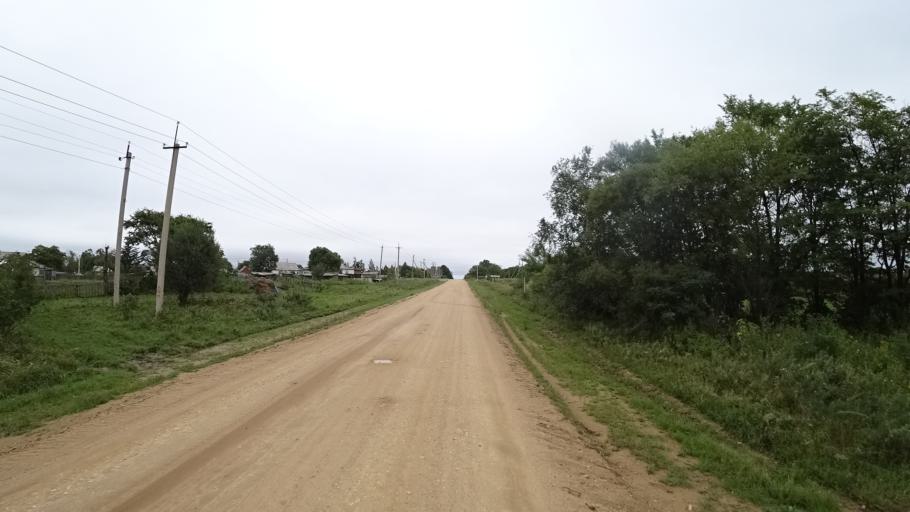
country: RU
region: Primorskiy
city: Monastyrishche
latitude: 44.0761
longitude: 132.5873
